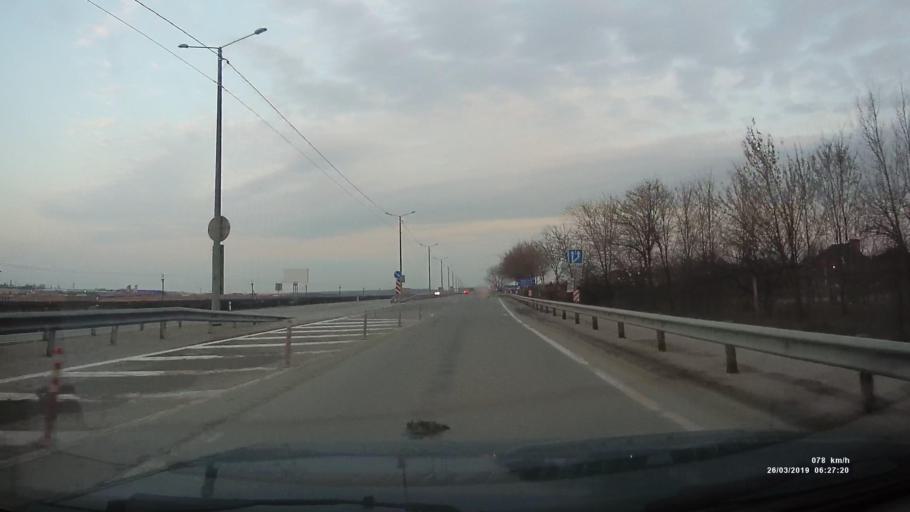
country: RU
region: Rostov
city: Severnyy
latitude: 47.2611
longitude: 39.6166
